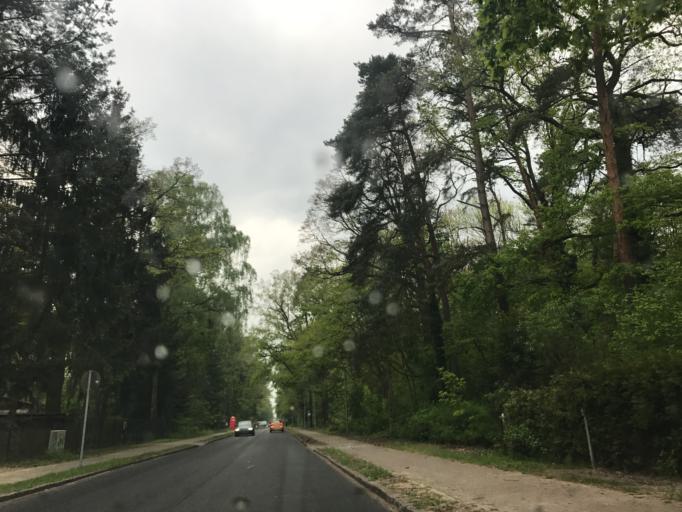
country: DE
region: Brandenburg
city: Falkensee
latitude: 52.5994
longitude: 13.1237
